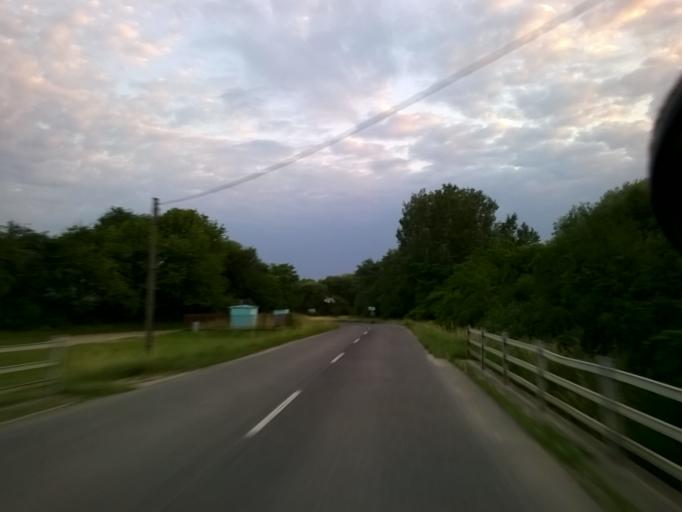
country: SK
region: Trnavsky
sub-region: Okres Senica
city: Senica
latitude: 48.7231
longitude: 17.3401
